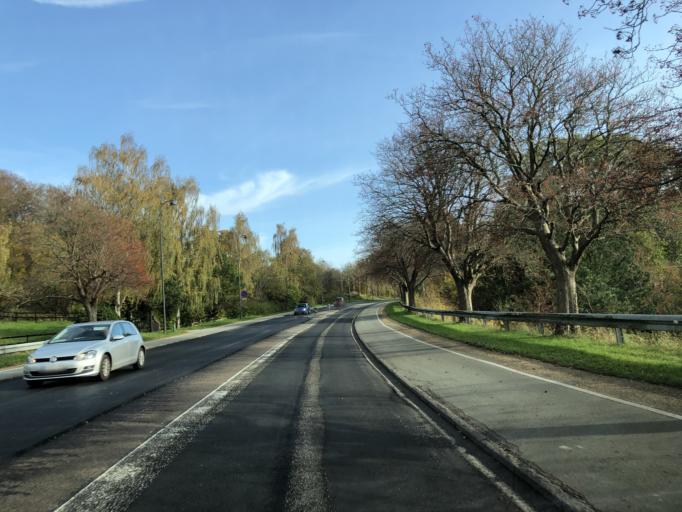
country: DK
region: Capital Region
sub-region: Rudersdal Kommune
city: Birkerod
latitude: 55.8374
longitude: 12.4491
